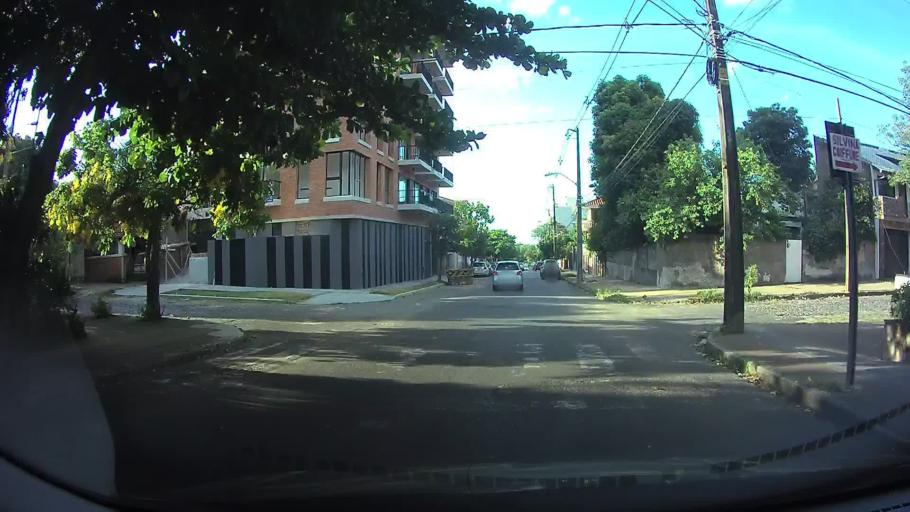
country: PY
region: Asuncion
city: Asuncion
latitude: -25.2780
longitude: -57.6038
